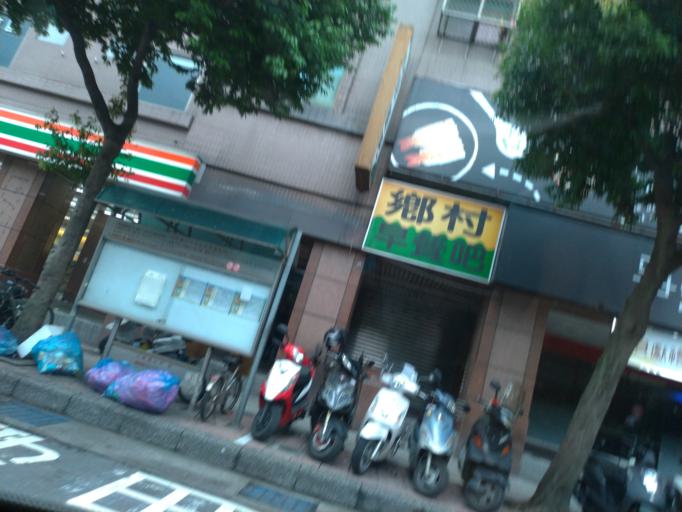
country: TW
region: Taiwan
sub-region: Taoyuan
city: Taoyuan
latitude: 24.9385
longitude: 121.3627
